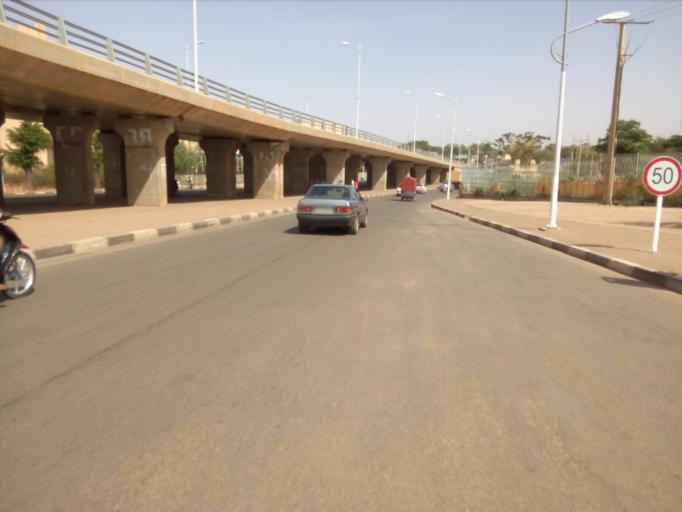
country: NE
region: Niamey
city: Niamey
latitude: 13.5090
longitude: 2.1073
